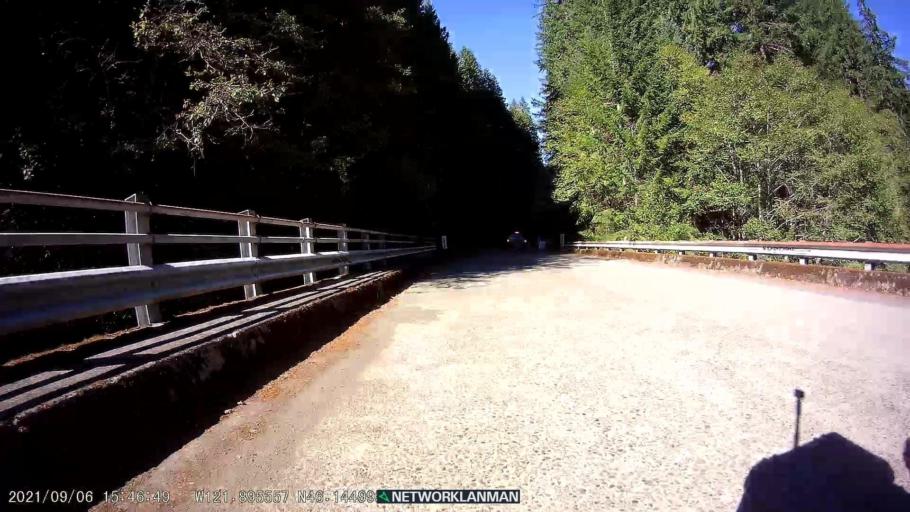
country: US
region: Washington
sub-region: Skamania County
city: Carson
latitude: 46.1447
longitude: -121.8958
